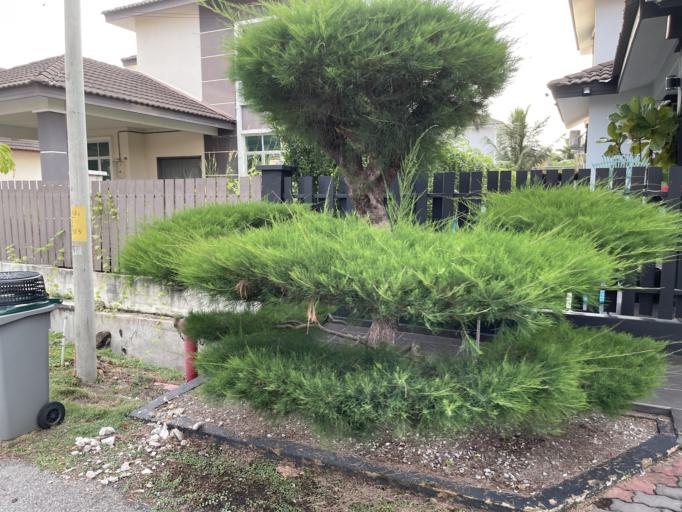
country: MY
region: Melaka
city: Alor Gajah
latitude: 2.3239
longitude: 102.2409
